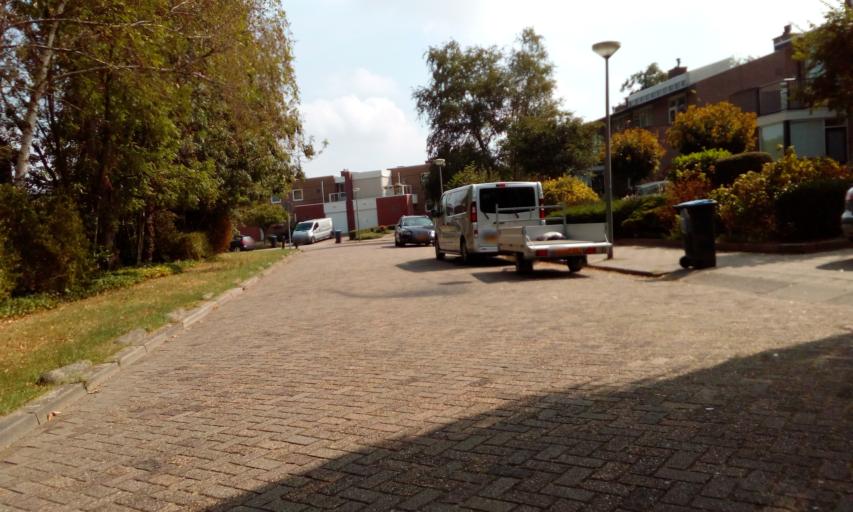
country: NL
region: South Holland
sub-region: Gemeente Schiedam
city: Schiedam
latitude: 51.9368
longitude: 4.3821
